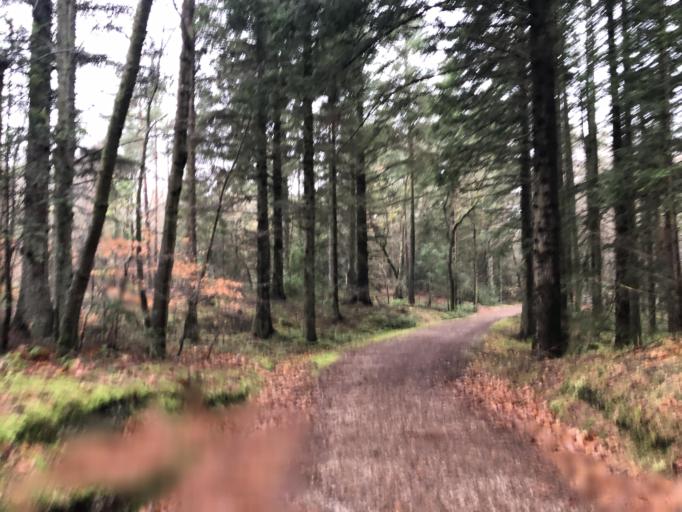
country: DK
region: Central Jutland
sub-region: Holstebro Kommune
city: Ulfborg
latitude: 56.2876
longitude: 8.1692
